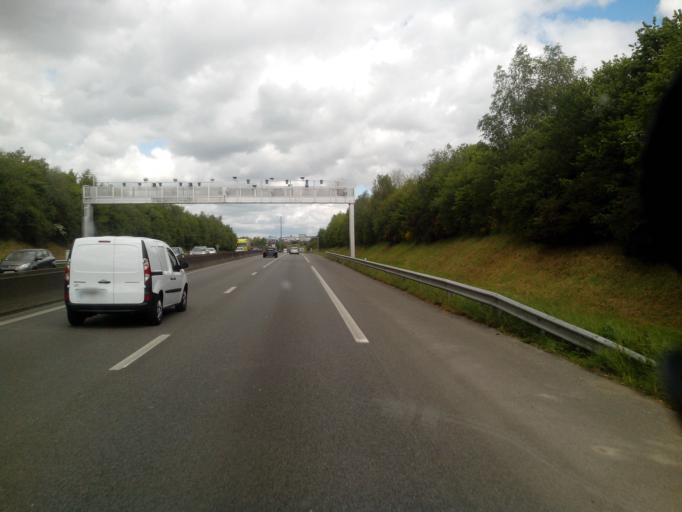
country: FR
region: Pays de la Loire
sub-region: Departement de la Loire-Atlantique
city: Orvault
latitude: 47.2455
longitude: -1.6216
